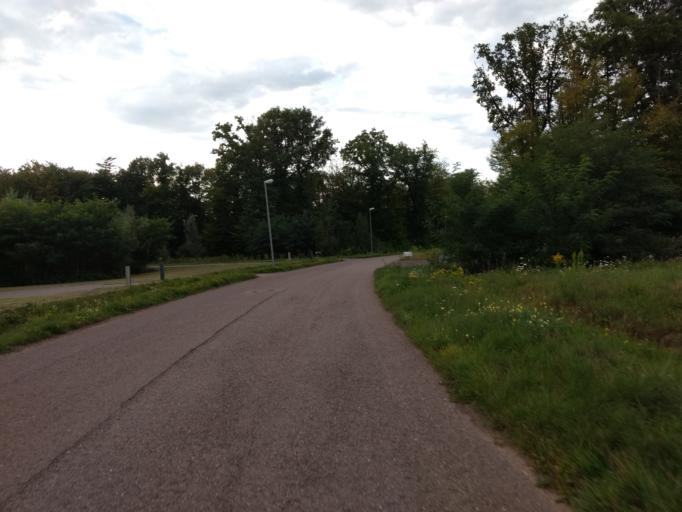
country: DE
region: Saarland
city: Nalbach
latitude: 49.3572
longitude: 6.7770
